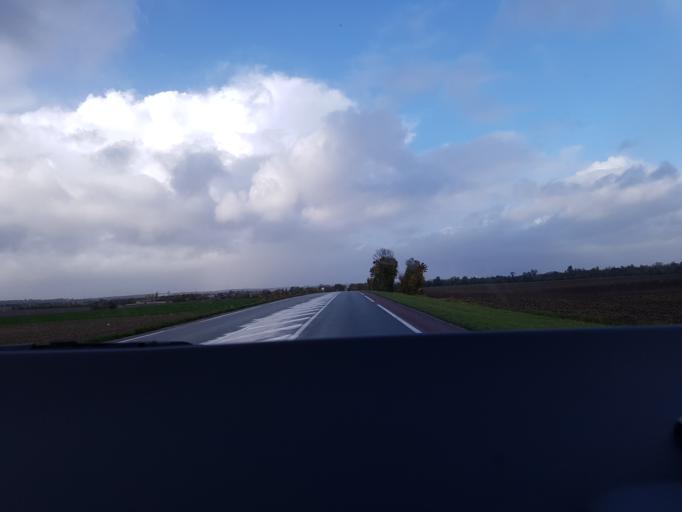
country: FR
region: Poitou-Charentes
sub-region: Departement de la Charente-Maritime
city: Les Gonds
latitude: 45.6858
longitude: -0.6118
